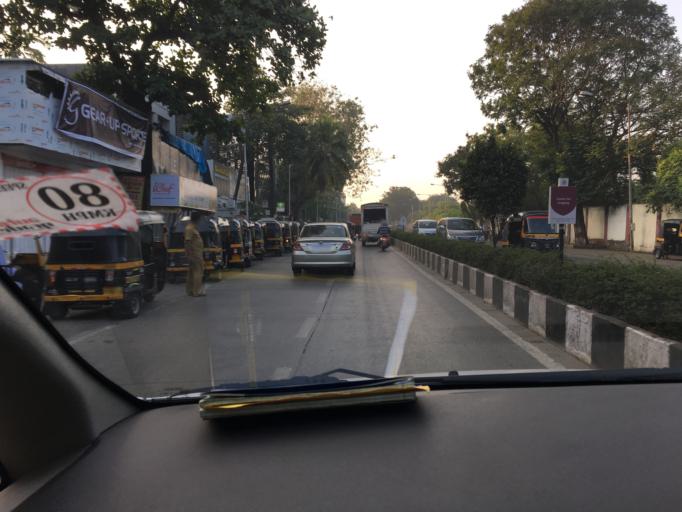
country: IN
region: Maharashtra
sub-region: Mumbai Suburban
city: Mumbai
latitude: 19.0997
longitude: 72.8395
